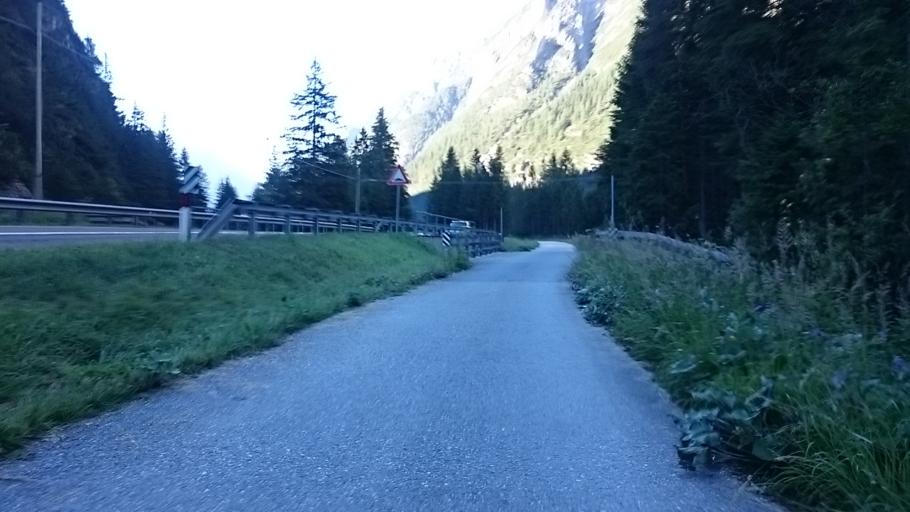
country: IT
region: Trentino-Alto Adige
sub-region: Bolzano
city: Dobbiaco
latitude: 46.6736
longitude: 12.2216
